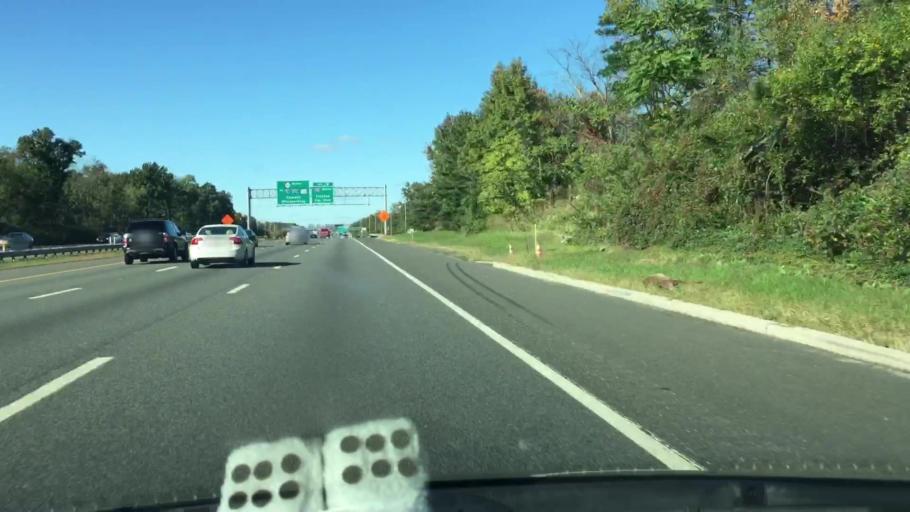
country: US
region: New Jersey
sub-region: Camden County
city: Bellmawr
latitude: 39.8462
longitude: -75.0947
